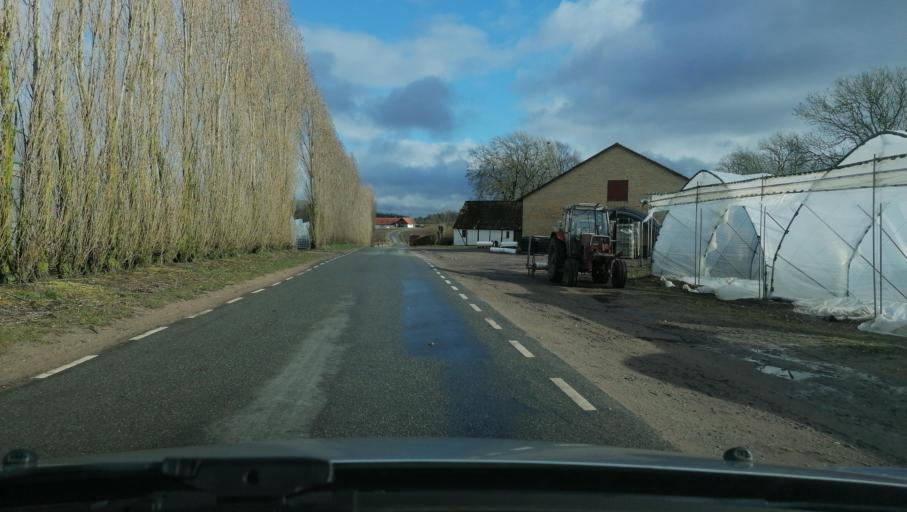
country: DK
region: Zealand
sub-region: Odsherred Kommune
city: Horve
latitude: 55.7528
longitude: 11.3929
